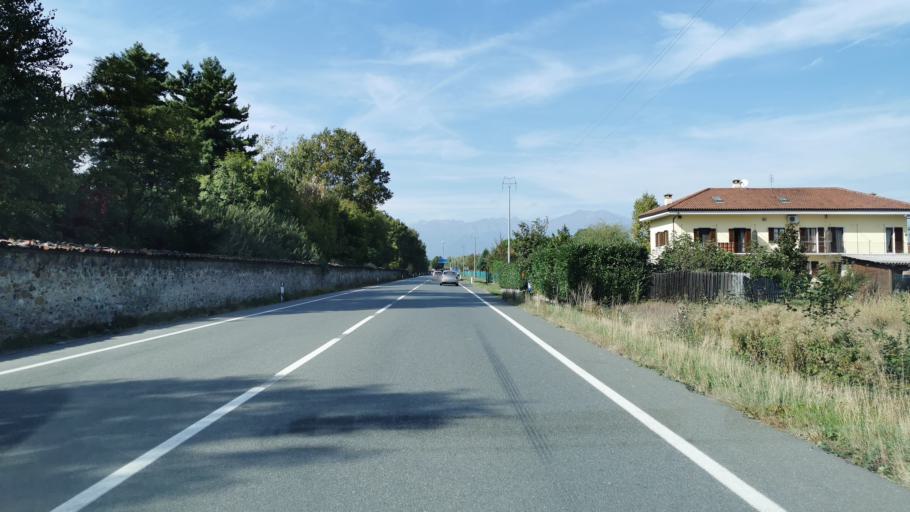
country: IT
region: Piedmont
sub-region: Provincia di Torino
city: Robassomero
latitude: 45.2034
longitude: 7.5539
